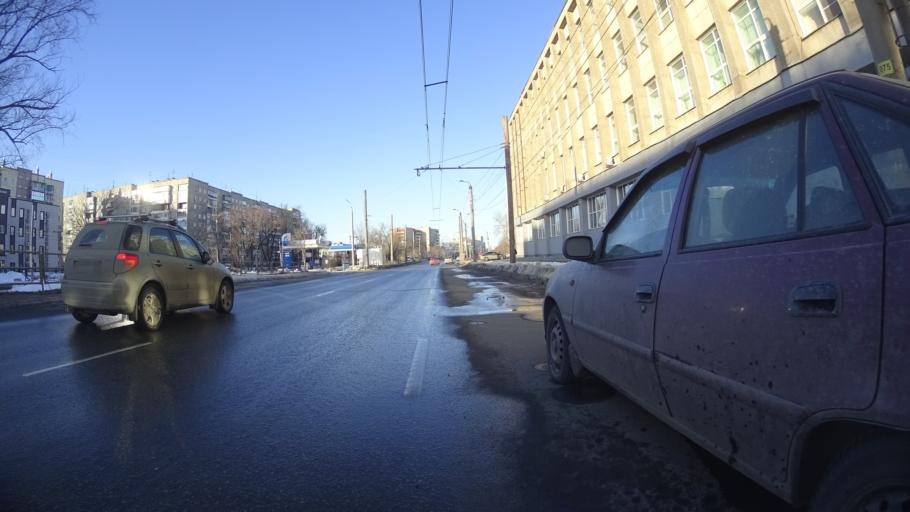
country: RU
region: Chelyabinsk
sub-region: Gorod Chelyabinsk
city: Chelyabinsk
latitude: 55.1233
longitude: 61.4746
